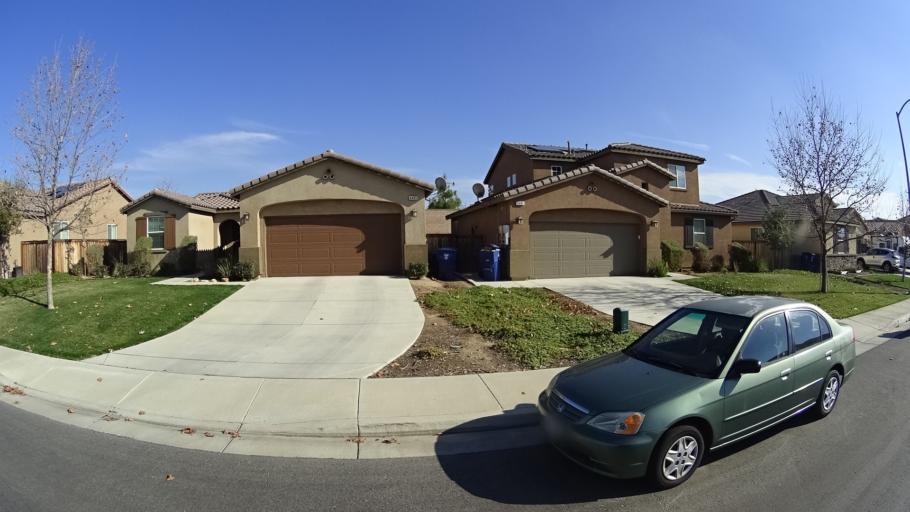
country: US
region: California
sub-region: Kern County
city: Oildale
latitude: 35.4115
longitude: -118.8971
